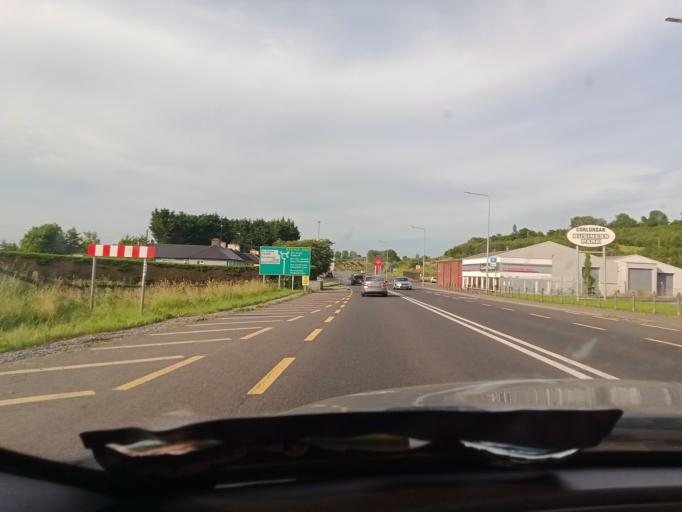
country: IE
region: Ulster
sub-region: An Cabhan
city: Cavan
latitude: 53.9634
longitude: -7.3581
